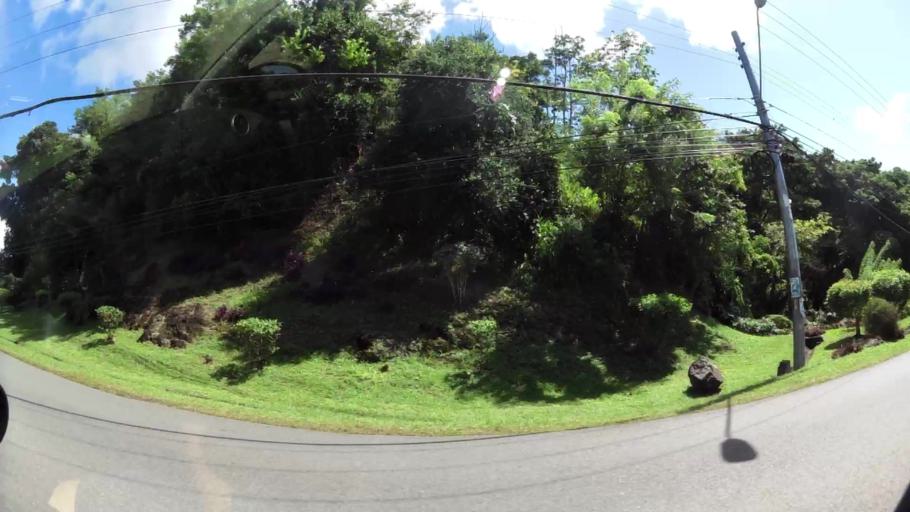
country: TT
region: Tobago
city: Scarborough
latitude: 11.2036
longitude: -60.7841
